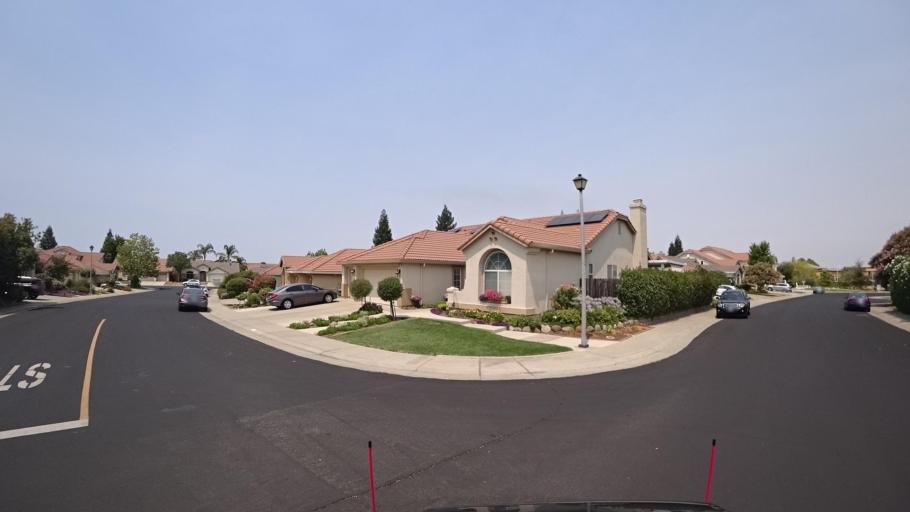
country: US
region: California
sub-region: Placer County
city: Rocklin
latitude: 38.8014
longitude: -121.2723
